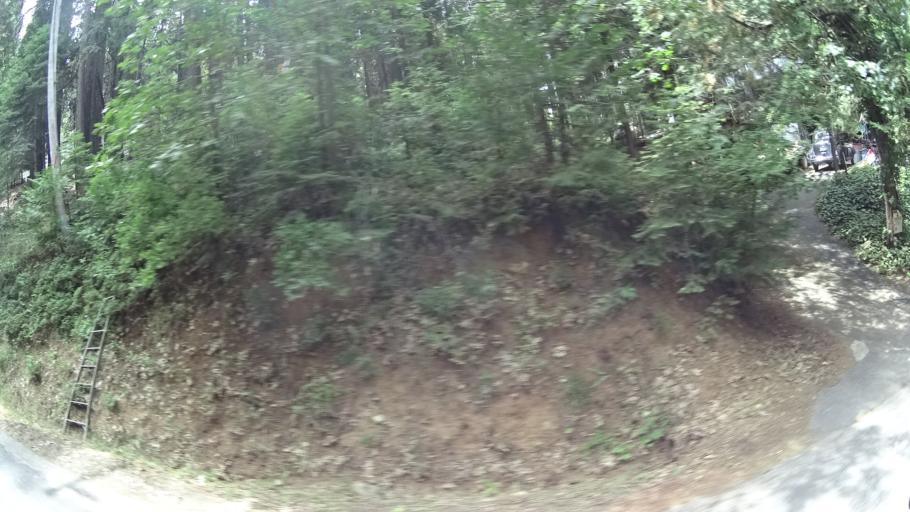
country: US
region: California
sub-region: Calaveras County
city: Arnold
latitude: 38.2507
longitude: -120.3520
